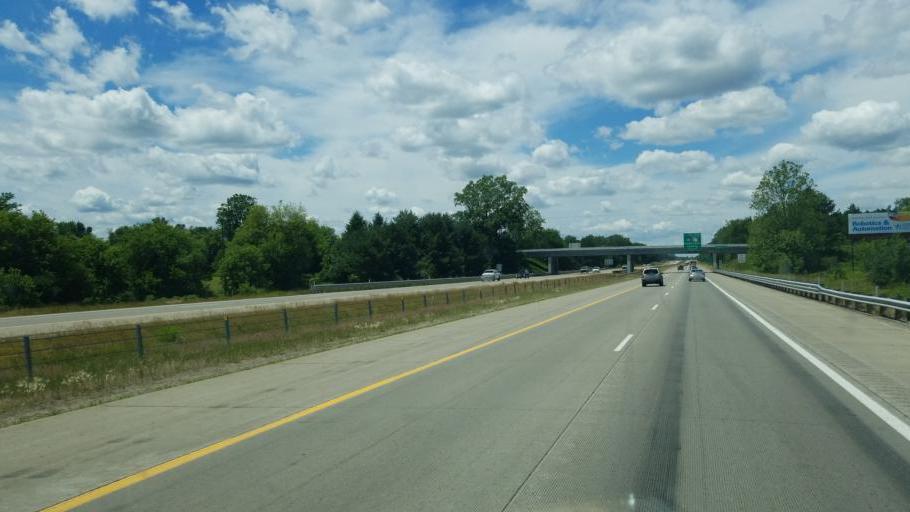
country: US
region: Michigan
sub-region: Ingham County
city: Okemos
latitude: 42.6781
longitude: -84.4599
